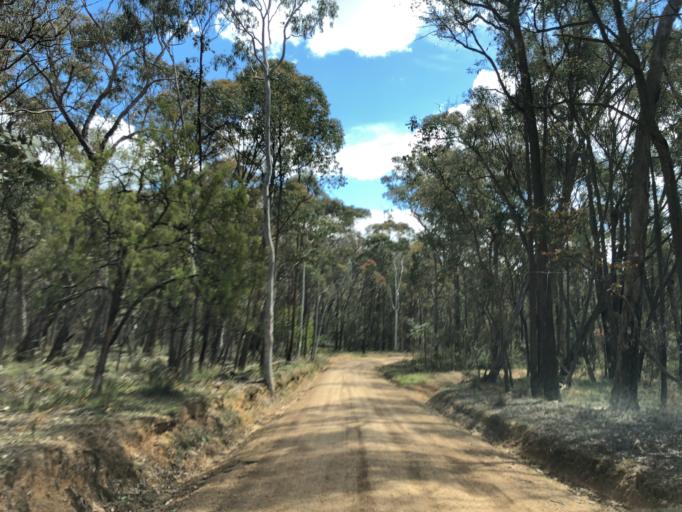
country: AU
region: Victoria
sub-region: Benalla
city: Benalla
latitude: -36.7496
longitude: 146.1610
